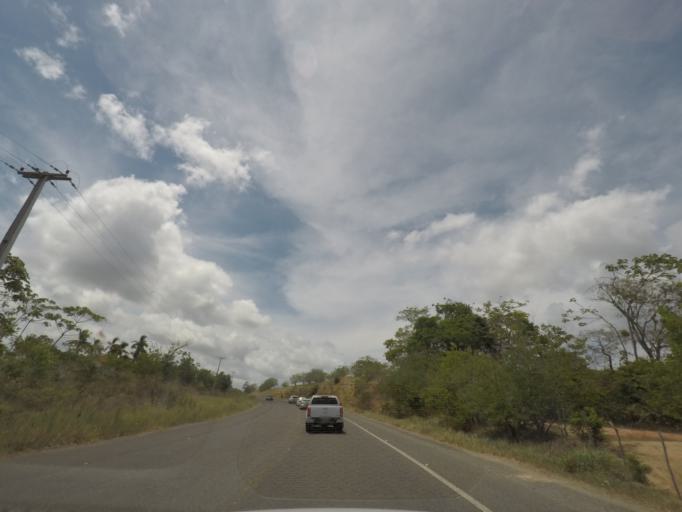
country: BR
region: Sergipe
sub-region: Indiaroba
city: Indiaroba
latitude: -11.5091
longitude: -37.5081
